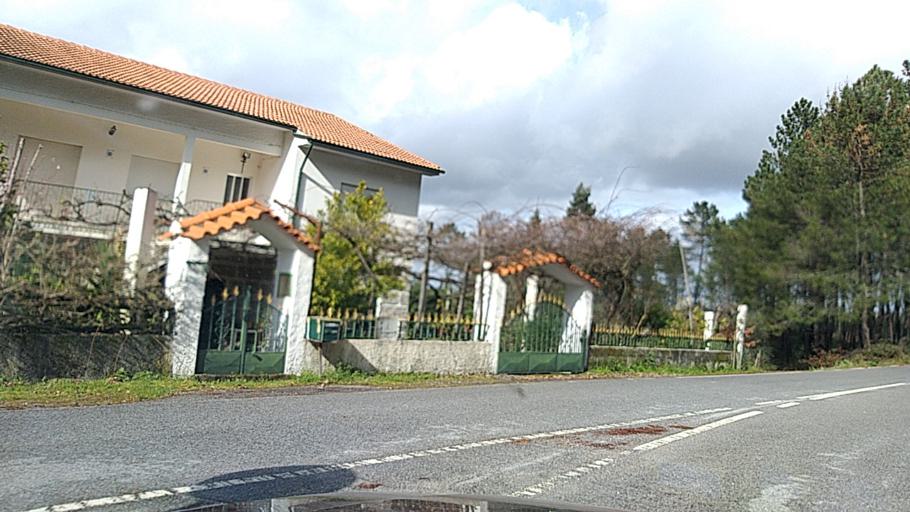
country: PT
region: Guarda
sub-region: Fornos de Algodres
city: Fornos de Algodres
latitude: 40.6597
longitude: -7.6389
